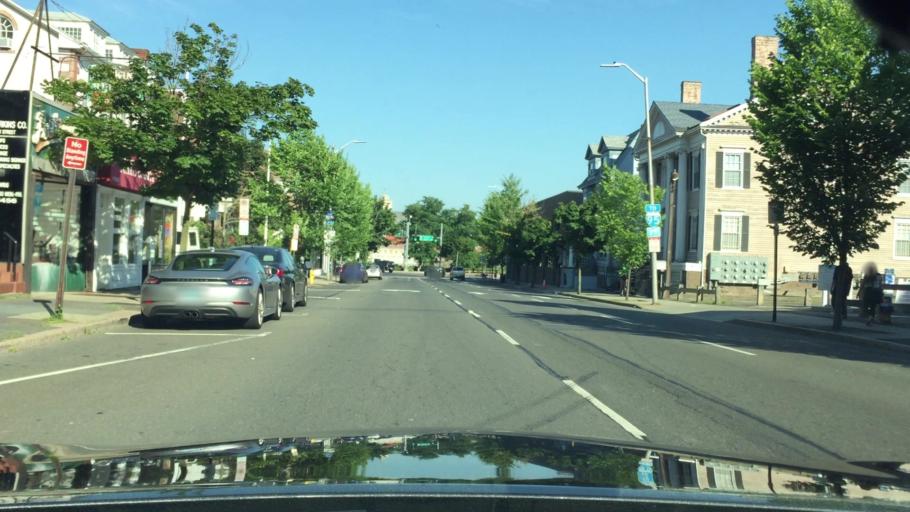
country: US
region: Connecticut
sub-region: New Haven County
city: New Haven
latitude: 41.3076
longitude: -72.9226
